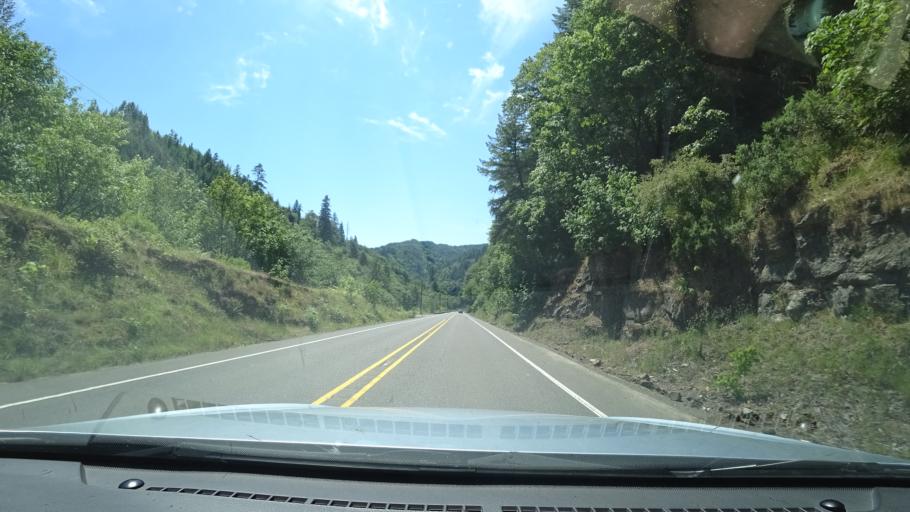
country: US
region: Oregon
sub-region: Lane County
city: Florence
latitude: 44.0131
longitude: -123.7748
